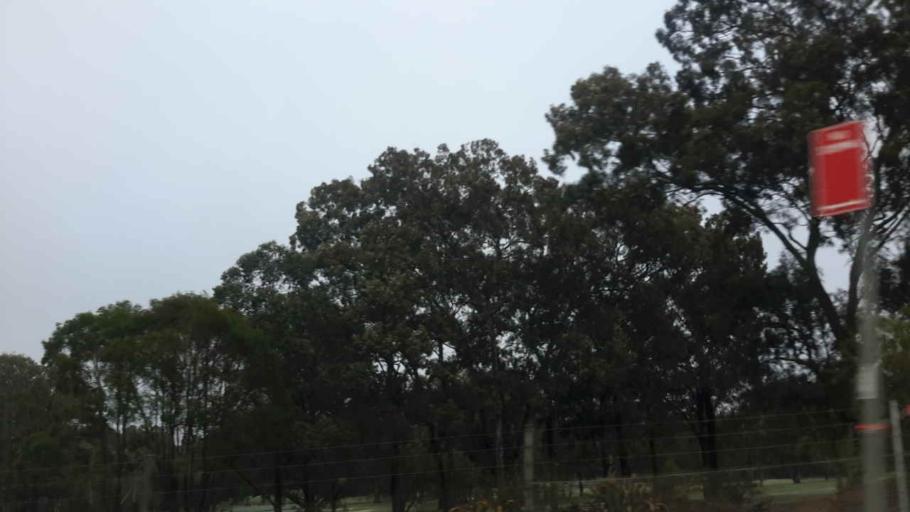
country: AU
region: New South Wales
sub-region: Penrith Municipality
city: Glenmore Park
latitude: -33.7929
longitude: 150.6990
